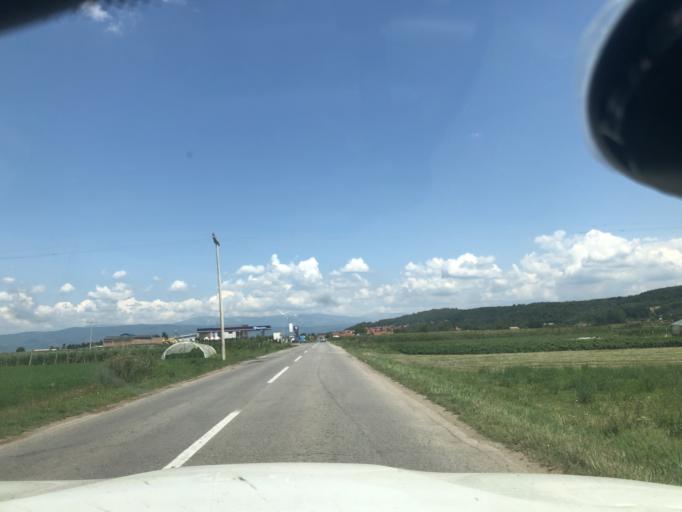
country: RS
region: Central Serbia
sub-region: Jablanicki Okrug
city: Leskovac
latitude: 42.9753
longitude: 21.8993
